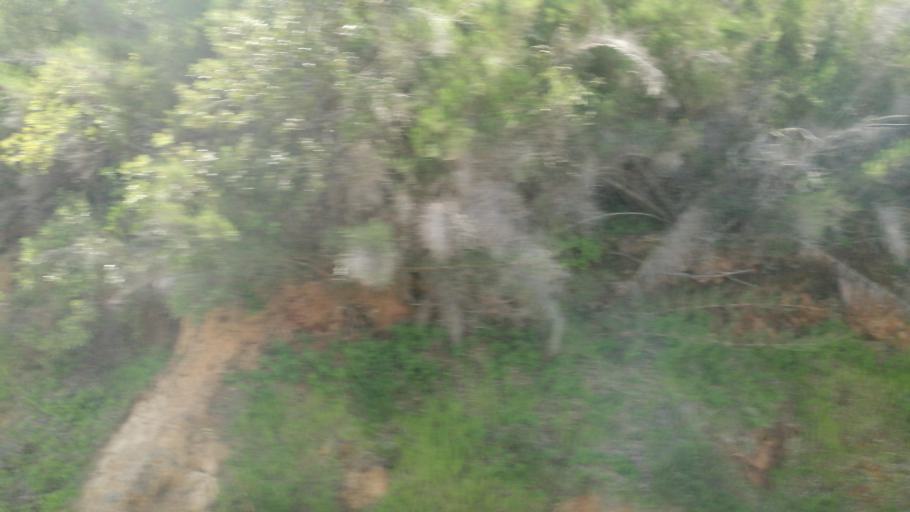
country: CL
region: Valparaiso
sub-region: Provincia de Marga Marga
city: Limache
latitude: -33.1828
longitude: -71.1767
